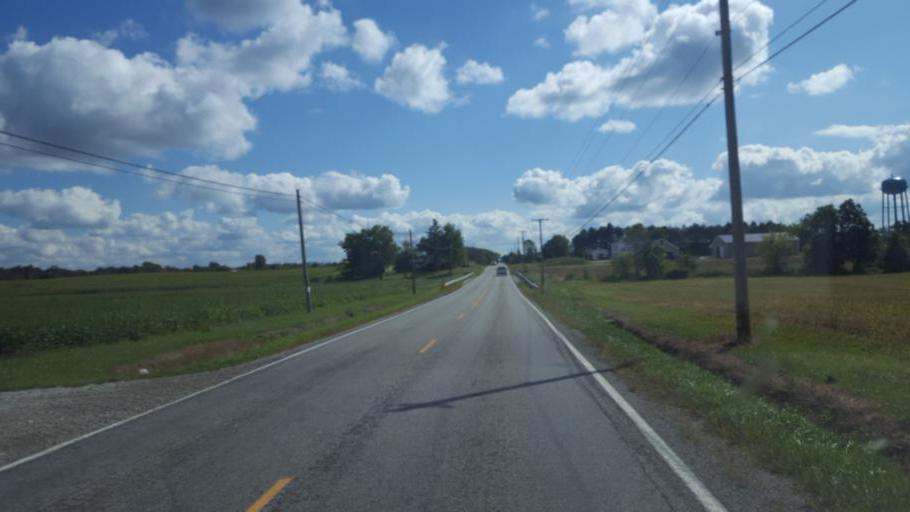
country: US
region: Ohio
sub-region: Lorain County
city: Lagrange
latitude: 41.2372
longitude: -82.1524
